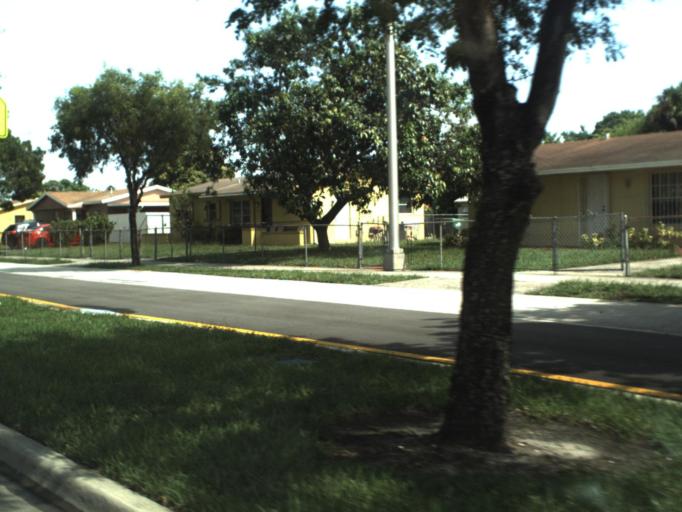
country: US
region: Florida
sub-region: Miami-Dade County
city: Carol City
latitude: 25.9403
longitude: -80.2594
